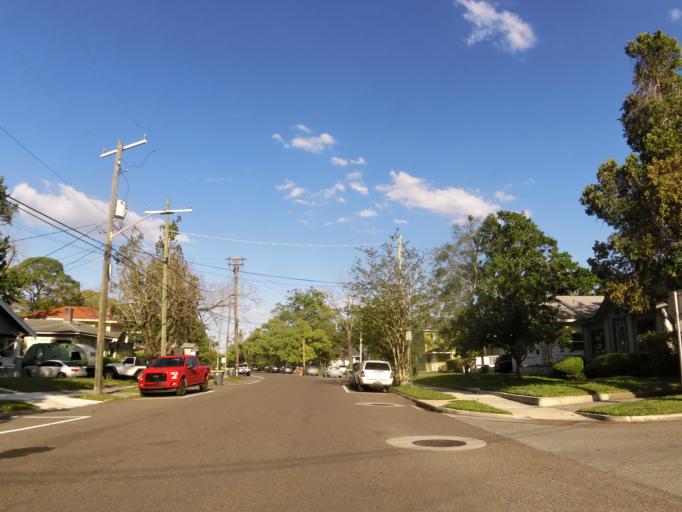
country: US
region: Florida
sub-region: Duval County
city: Jacksonville
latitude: 30.3141
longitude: -81.6928
